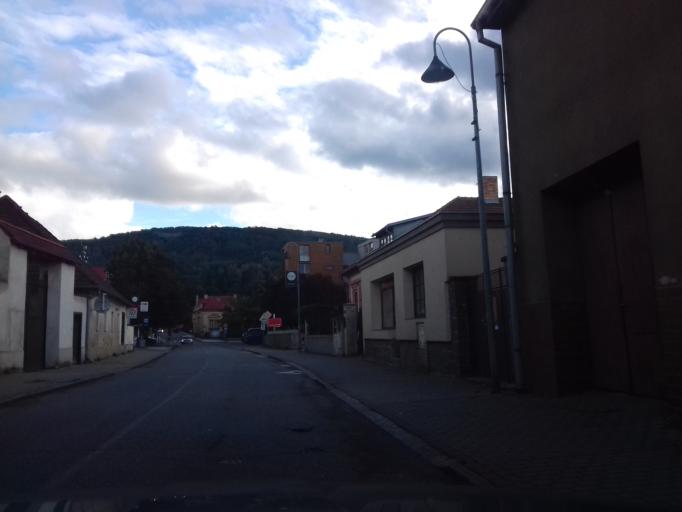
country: CZ
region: Central Bohemia
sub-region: Okres Praha-Zapad
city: Dobrichovice
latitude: 49.9281
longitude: 14.2741
